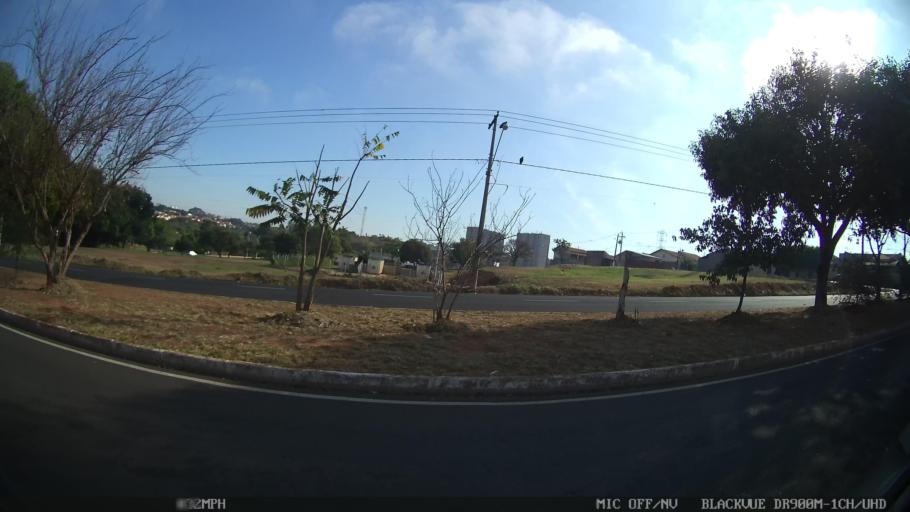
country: BR
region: Sao Paulo
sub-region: Sao Jose Do Rio Preto
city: Sao Jose do Rio Preto
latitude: -20.7938
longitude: -49.4226
